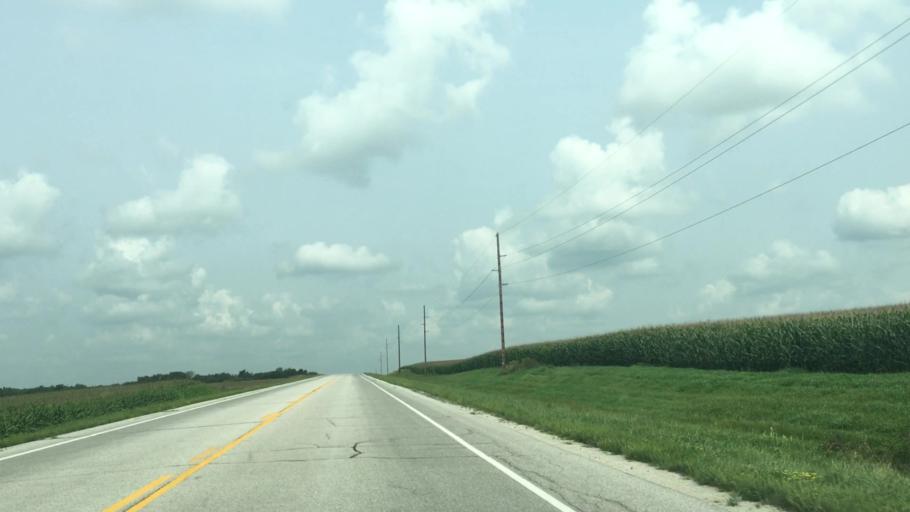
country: US
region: Minnesota
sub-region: Fillmore County
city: Harmony
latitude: 43.5677
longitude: -91.9298
